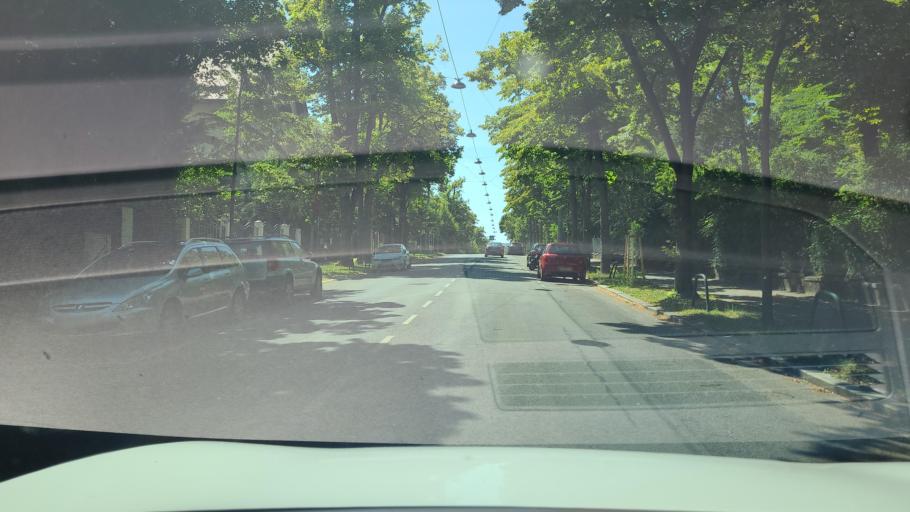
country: AT
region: Vienna
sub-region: Wien Stadt
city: Vienna
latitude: 48.2338
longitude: 16.3359
